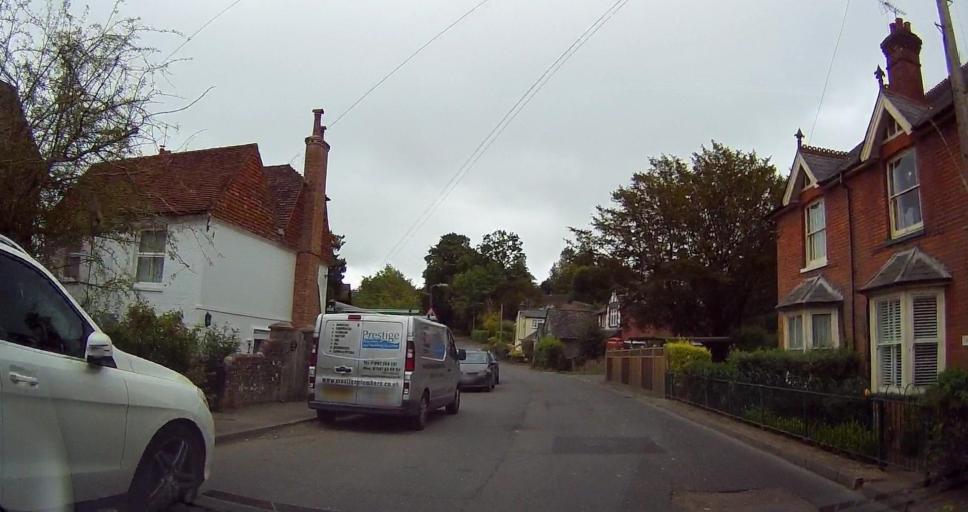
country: GB
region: England
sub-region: East Sussex
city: Wadhurst
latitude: 51.0661
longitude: 0.3286
